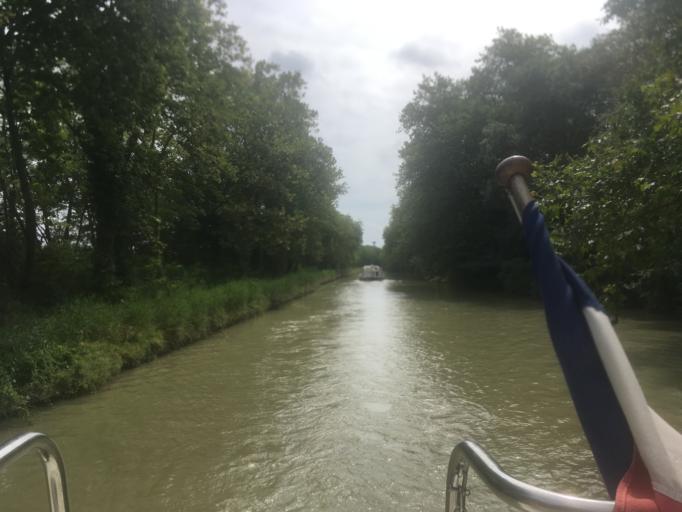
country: FR
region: Languedoc-Roussillon
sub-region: Departement de l'Aude
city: Villepinte
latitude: 43.2770
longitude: 2.0635
